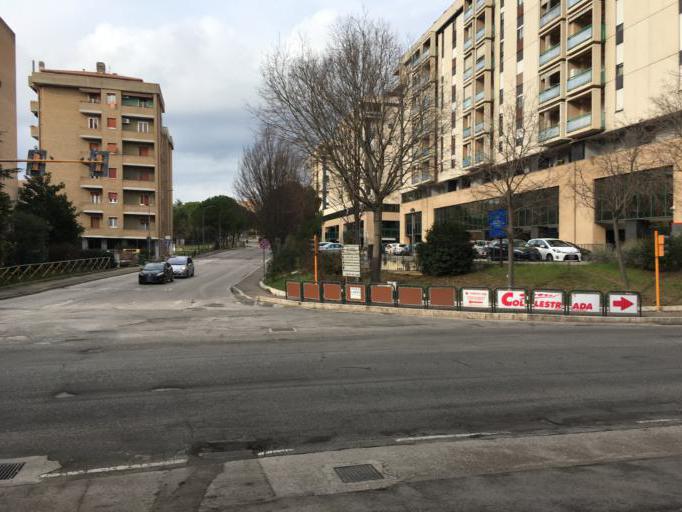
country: IT
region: Umbria
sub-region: Provincia di Perugia
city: Perugia
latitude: 43.1001
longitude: 12.3747
